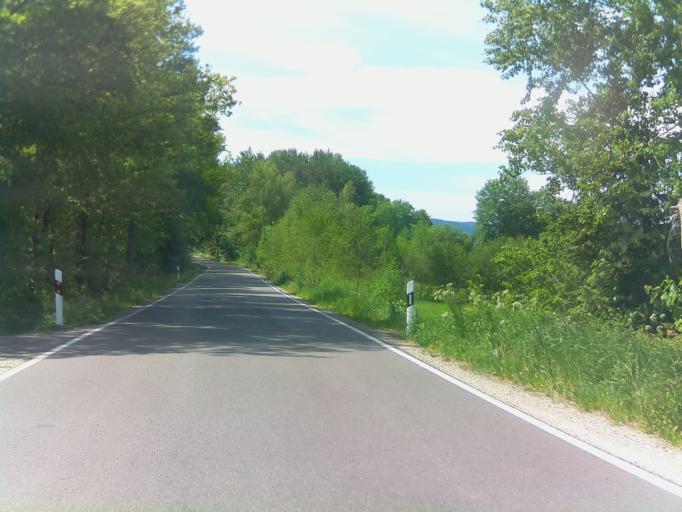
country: DE
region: Thuringia
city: Martinroda
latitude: 50.7232
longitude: 10.9075
